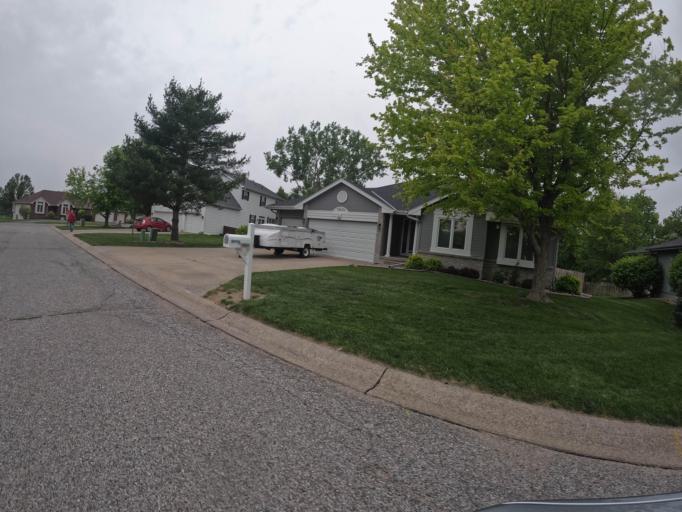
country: US
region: Nebraska
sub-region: Sarpy County
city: Offutt Air Force Base
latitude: 41.0497
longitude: -95.9733
